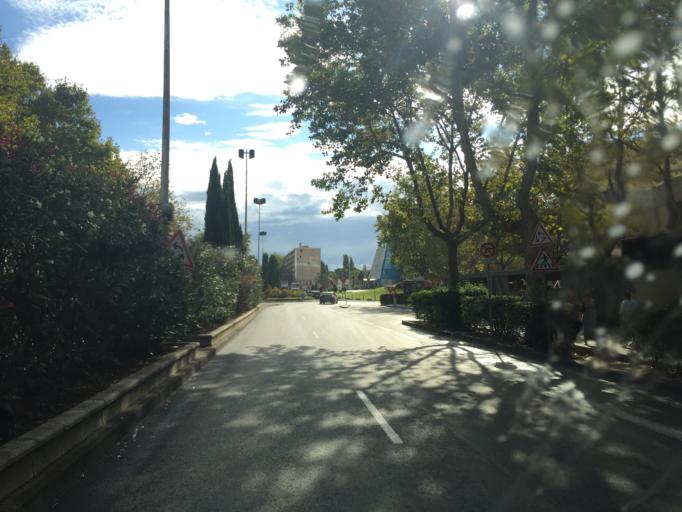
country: FR
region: Provence-Alpes-Cote d'Azur
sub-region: Departement des Bouches-du-Rhone
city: Aix-en-Provence
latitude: 43.5240
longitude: 5.4339
